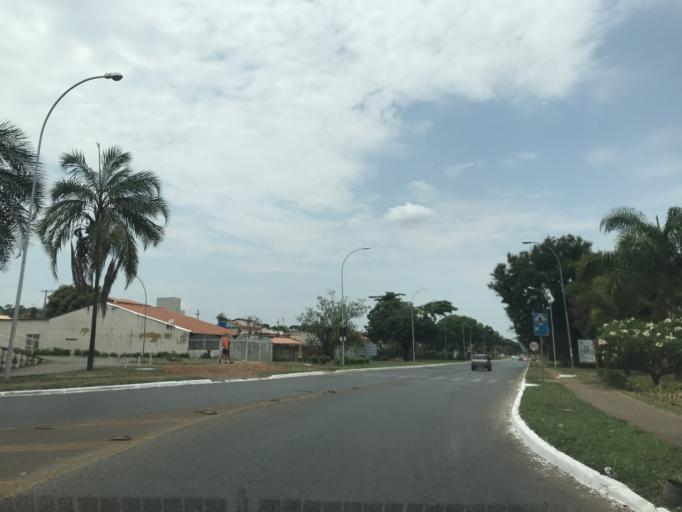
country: BR
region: Federal District
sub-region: Brasilia
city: Brasilia
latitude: -15.6477
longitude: -47.8034
